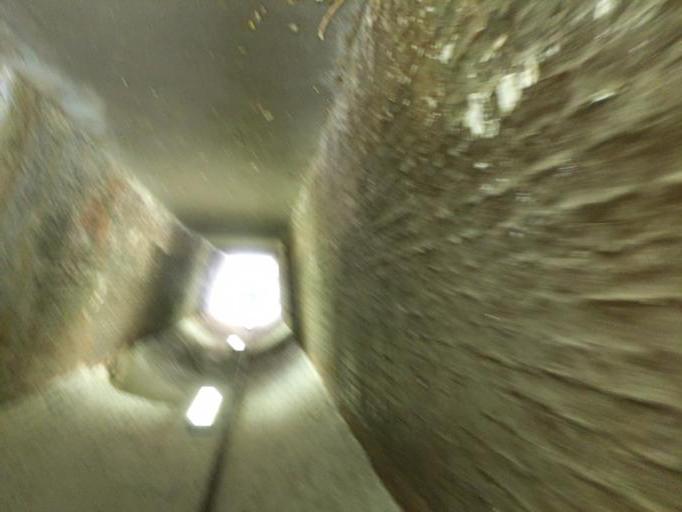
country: GB
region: England
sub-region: Surrey
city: Esher
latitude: 51.3800
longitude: -0.3557
